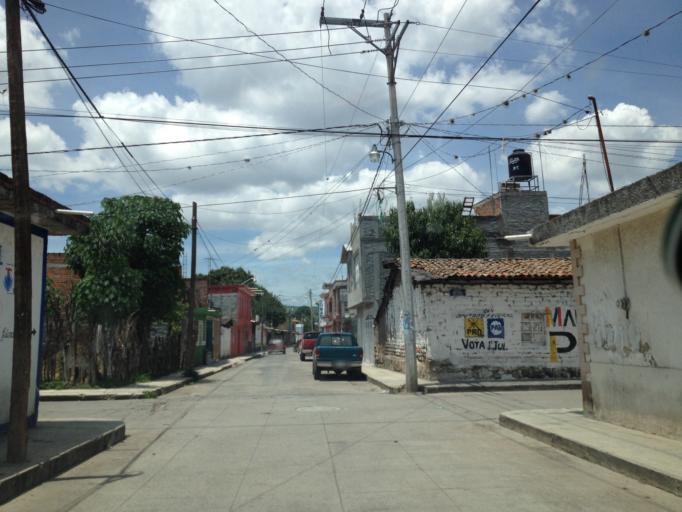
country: MX
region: Michoacan
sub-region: Tarimbaro
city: El Colegio
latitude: 19.7933
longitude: -101.1748
